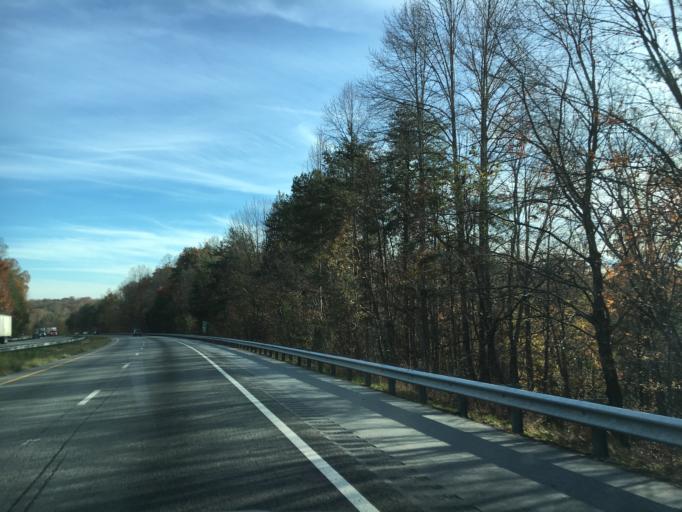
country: US
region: South Carolina
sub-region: Spartanburg County
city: Landrum
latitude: 35.2061
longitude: -82.1811
